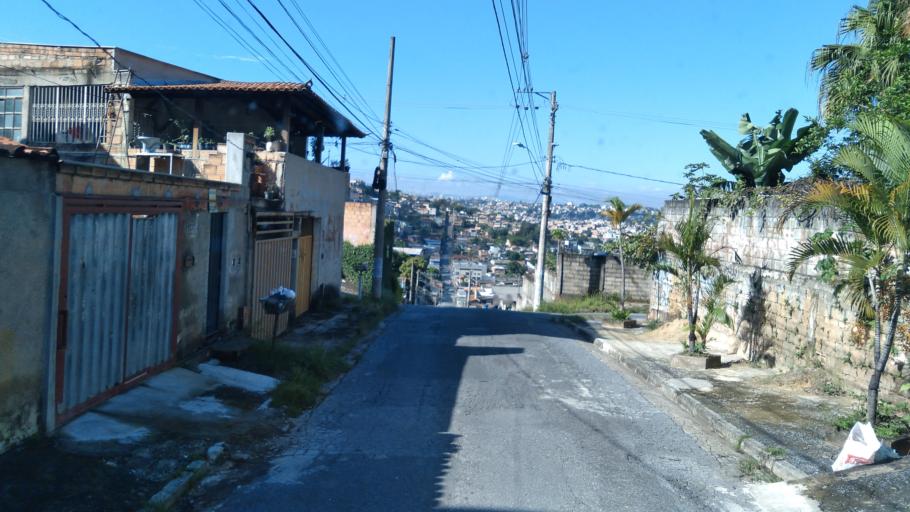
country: BR
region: Minas Gerais
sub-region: Santa Luzia
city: Santa Luzia
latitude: -19.8294
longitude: -43.9003
